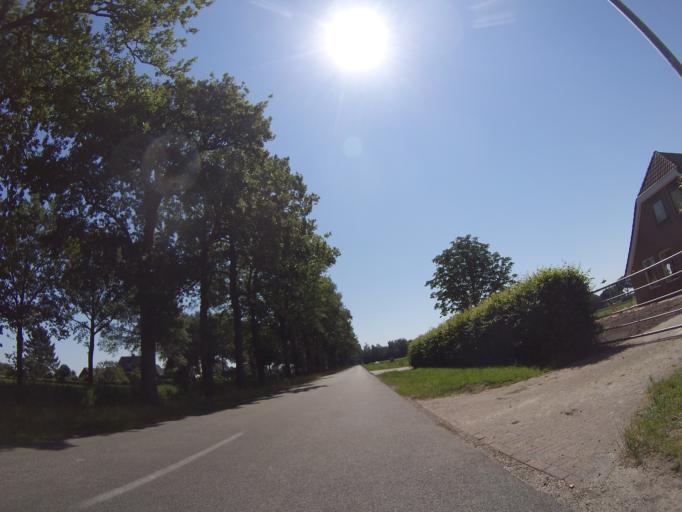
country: NL
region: Drenthe
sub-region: Gemeente Coevorden
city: Sleen
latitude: 52.8434
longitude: 6.7861
